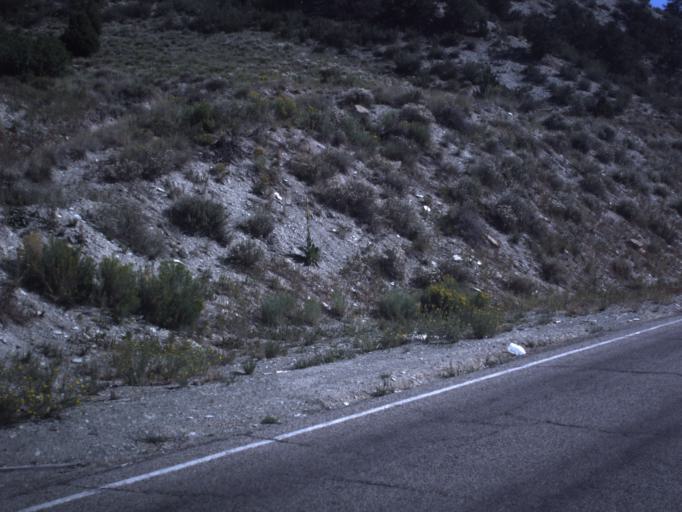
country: US
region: Utah
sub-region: Carbon County
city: Helper
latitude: 39.9140
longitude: -110.6961
